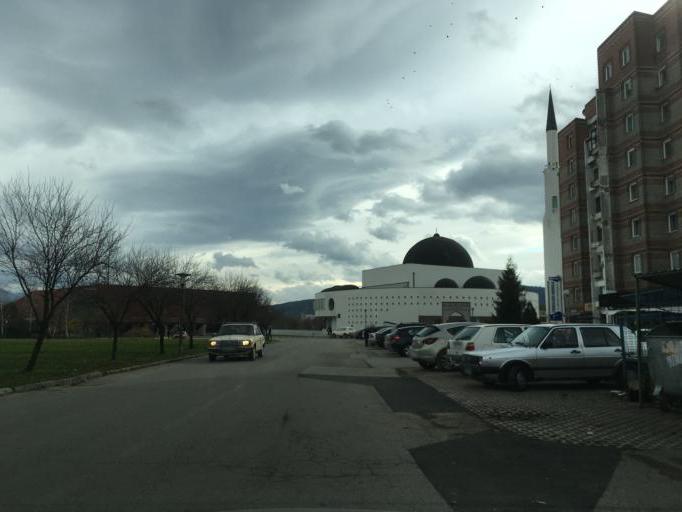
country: BA
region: Federation of Bosnia and Herzegovina
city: Bugojno
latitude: 44.0528
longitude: 17.4445
